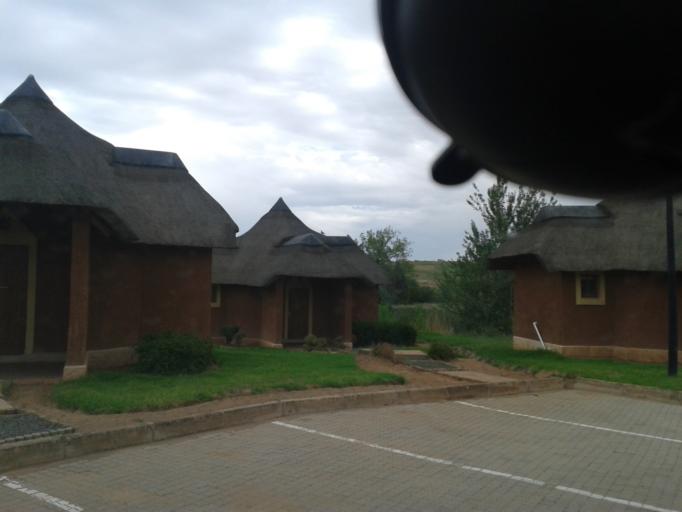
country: LS
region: Maseru
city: Maseru
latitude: -29.3435
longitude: 27.6622
